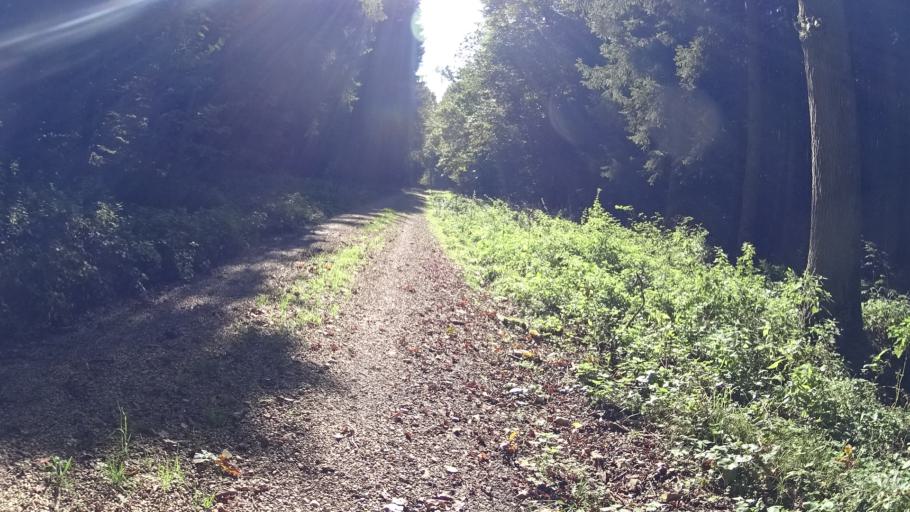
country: DE
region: Bavaria
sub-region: Upper Bavaria
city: Hitzhofen
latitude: 48.8814
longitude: 11.3062
